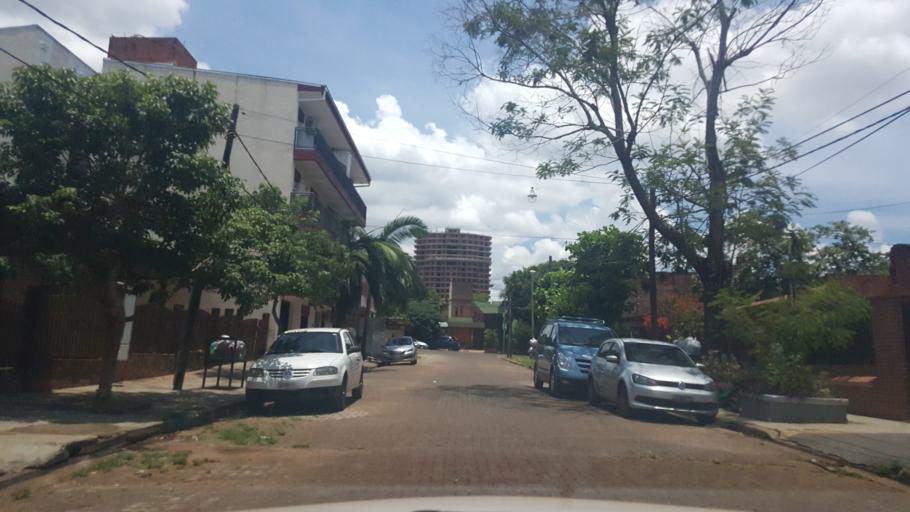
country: AR
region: Misiones
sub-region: Departamento de Capital
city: Posadas
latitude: -27.3611
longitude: -55.9036
